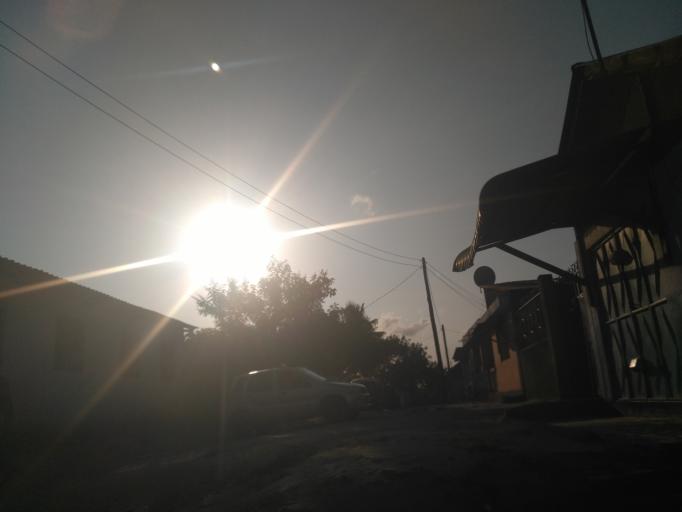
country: TZ
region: Dar es Salaam
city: Dar es Salaam
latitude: -6.9040
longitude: 39.2674
